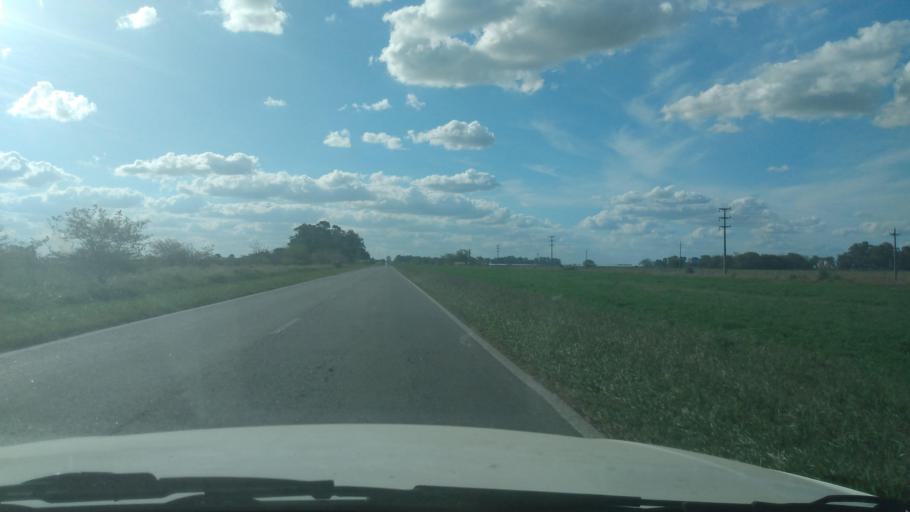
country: AR
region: Buenos Aires
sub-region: Partido de Navarro
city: Navarro
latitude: -34.9089
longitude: -59.3316
